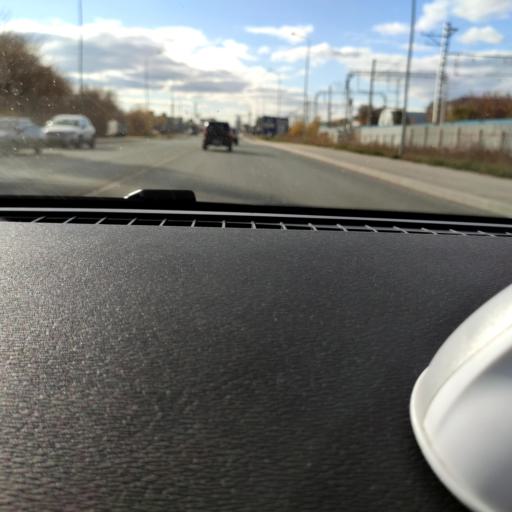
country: RU
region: Samara
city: Samara
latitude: 53.1794
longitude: 50.2066
